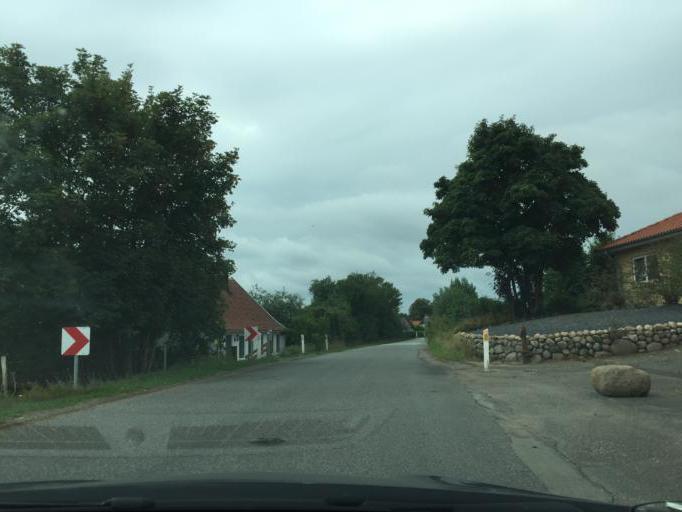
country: DK
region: South Denmark
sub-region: Assens Kommune
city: Harby
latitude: 55.1956
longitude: 10.0863
